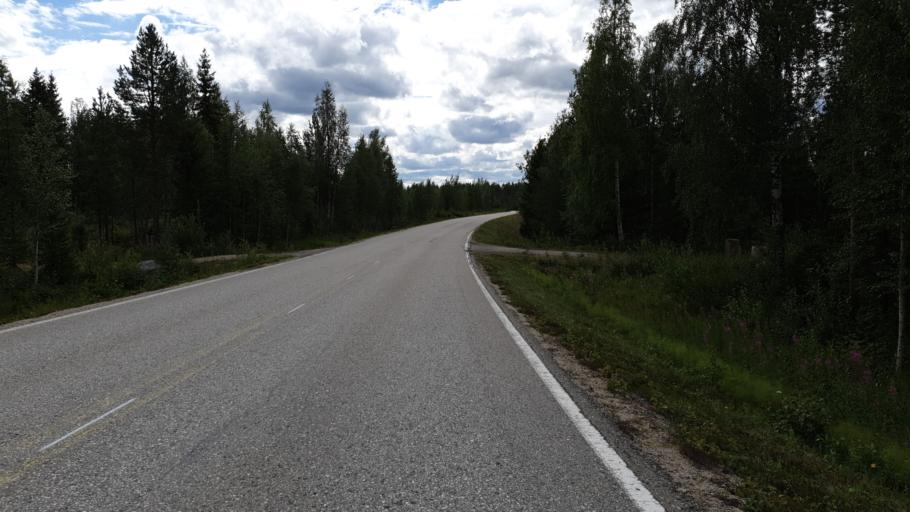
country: FI
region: Kainuu
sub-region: Kehys-Kainuu
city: Kuhmo
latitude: 64.4028
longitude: 29.8225
